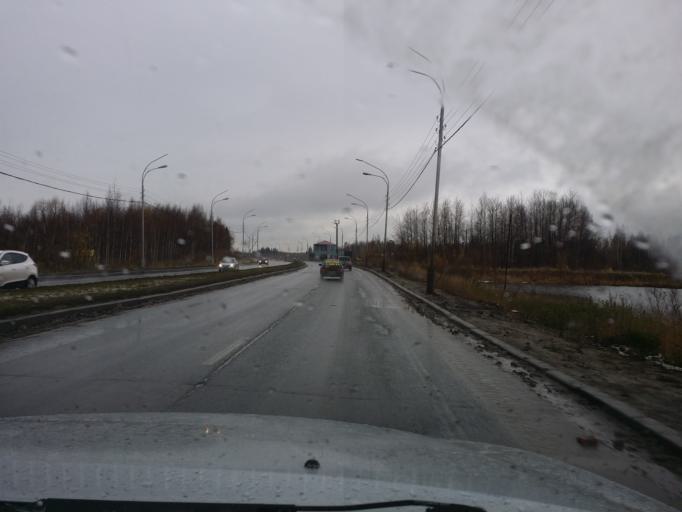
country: RU
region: Khanty-Mansiyskiy Avtonomnyy Okrug
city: Nizhnevartovsk
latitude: 60.9751
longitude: 76.5204
